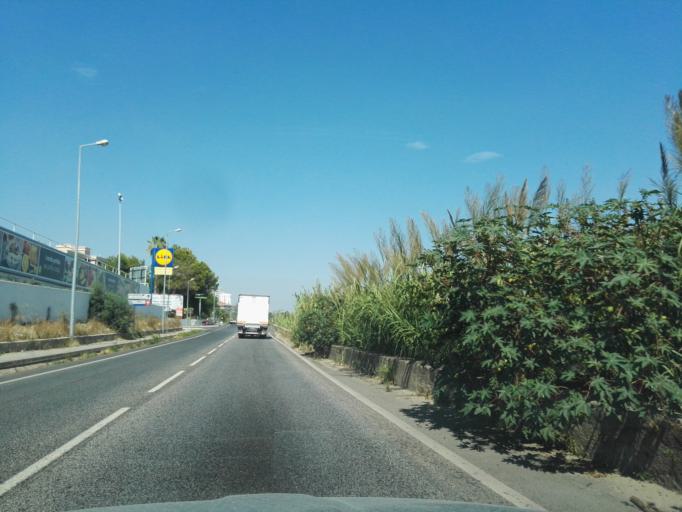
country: PT
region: Lisbon
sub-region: Vila Franca de Xira
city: Povoa de Santa Iria
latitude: 38.8512
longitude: -9.0743
